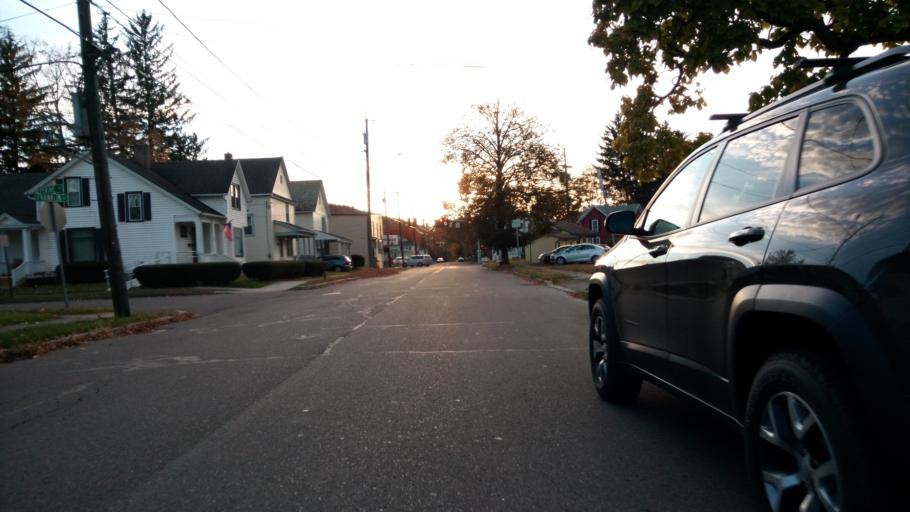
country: US
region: New York
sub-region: Chemung County
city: Elmira
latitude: 42.0750
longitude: -76.8116
